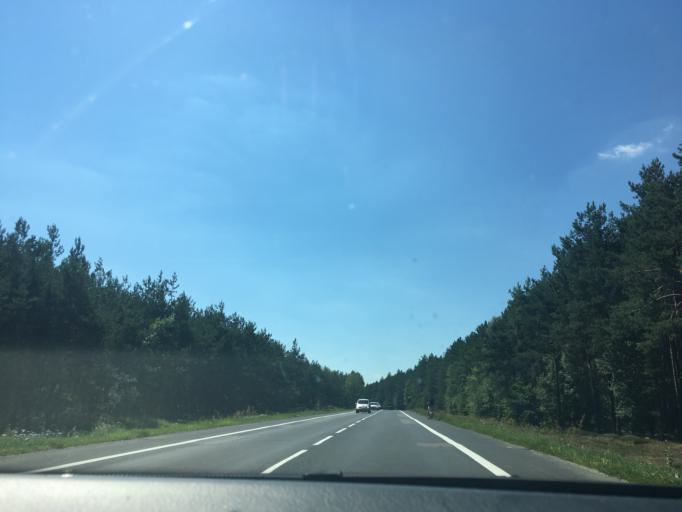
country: PL
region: Subcarpathian Voivodeship
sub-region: Powiat nizanski
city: Jarocin
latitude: 50.6034
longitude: 22.2778
